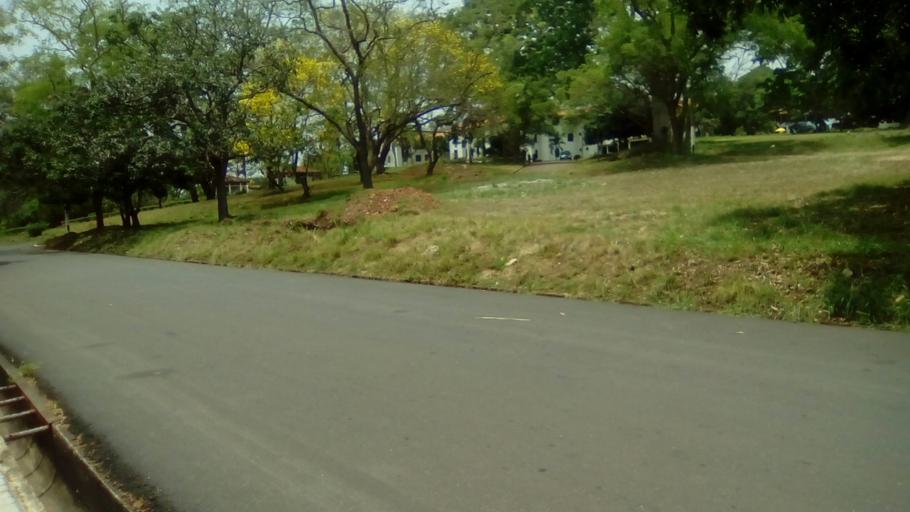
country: GH
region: Greater Accra
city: Medina Estates
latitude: 5.6519
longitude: -0.1906
